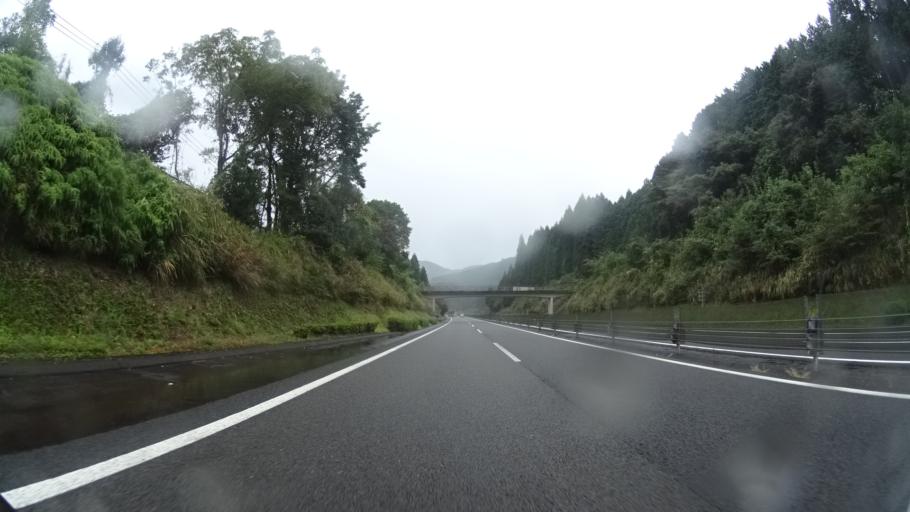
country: JP
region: Kagoshima
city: Okuchi-shinohara
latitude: 31.9575
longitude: 130.7390
